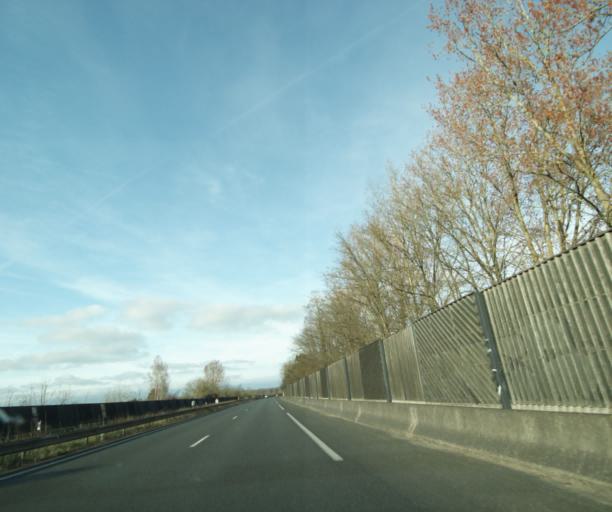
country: FR
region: Ile-de-France
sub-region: Departement des Yvelines
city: Le Perray-en-Yvelines
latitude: 48.6944
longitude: 1.8452
